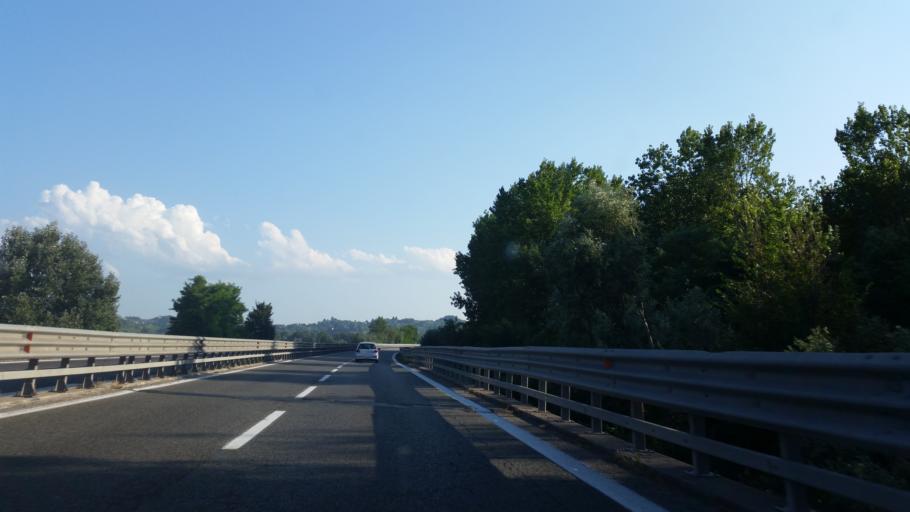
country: IT
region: Piedmont
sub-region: Provincia di Asti
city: Azzano d'Asti
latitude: 44.8974
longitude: 8.2462
